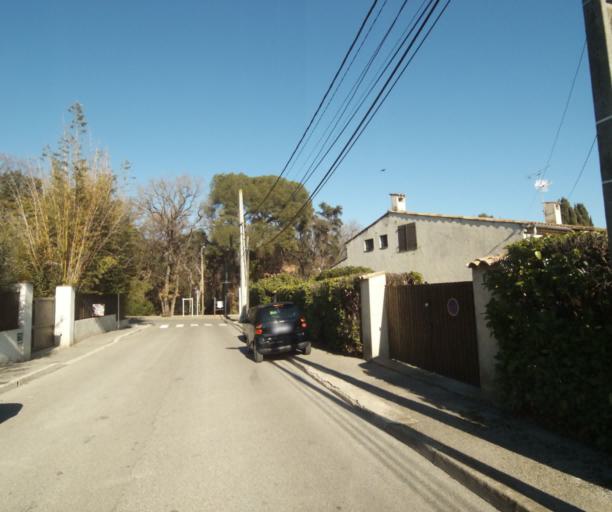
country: FR
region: Provence-Alpes-Cote d'Azur
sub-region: Departement des Alpes-Maritimes
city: Biot
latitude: 43.6196
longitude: 7.1232
